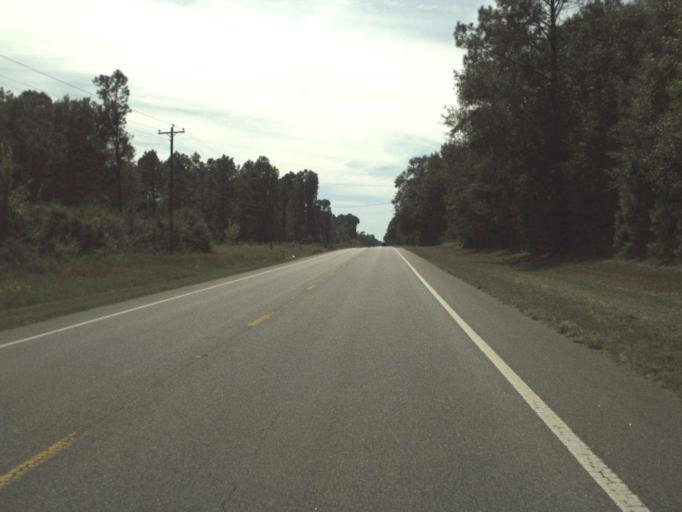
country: US
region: Florida
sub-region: Washington County
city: Chipley
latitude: 30.6909
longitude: -85.5662
